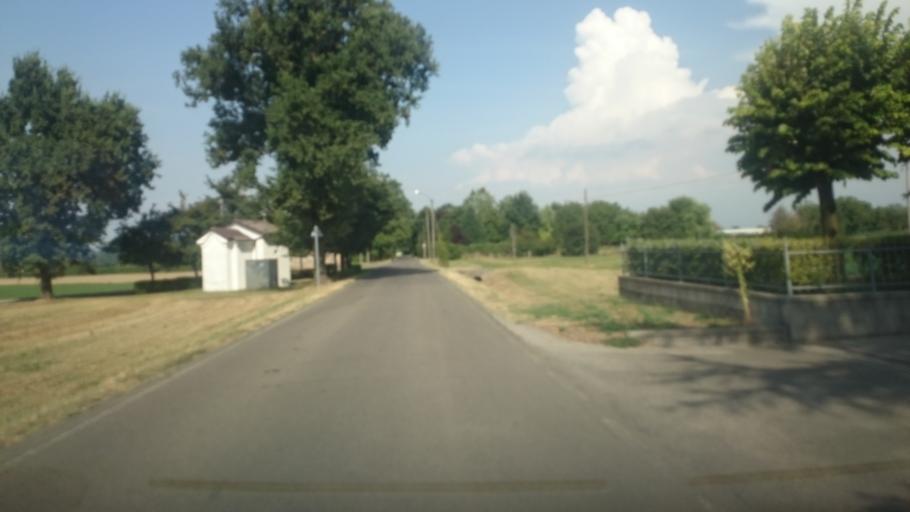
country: IT
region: Emilia-Romagna
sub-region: Provincia di Reggio Emilia
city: Bagno
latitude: 44.6474
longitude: 10.7534
